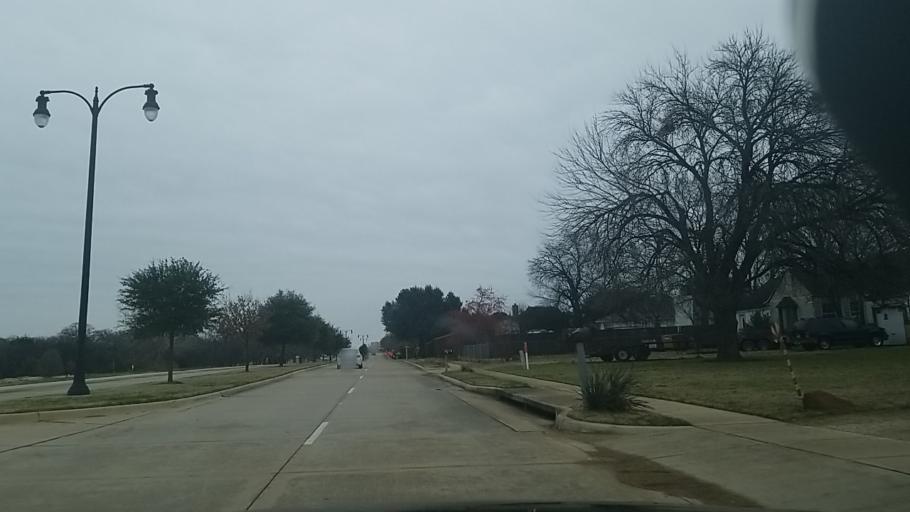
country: US
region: Texas
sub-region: Denton County
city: Corinth
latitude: 33.1447
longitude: -97.0639
